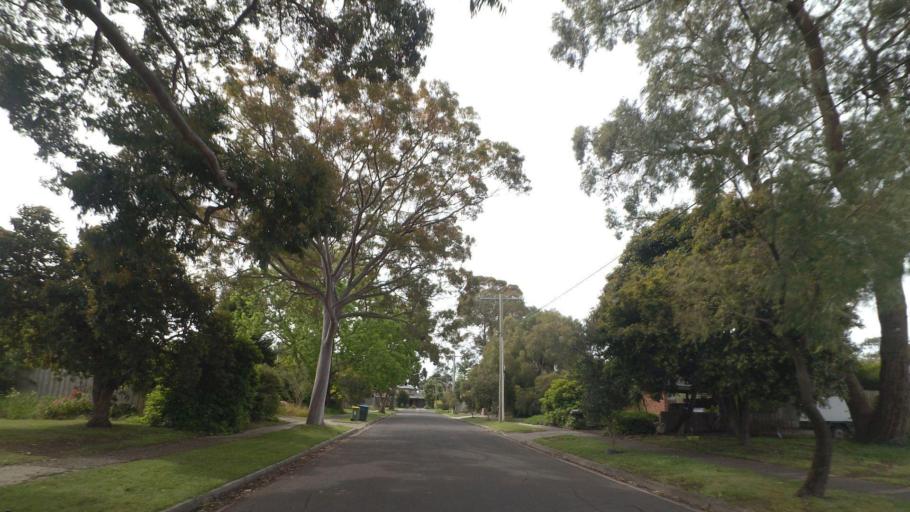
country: AU
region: Victoria
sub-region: Knox
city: Knoxfield
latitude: -37.8877
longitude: 145.2538
